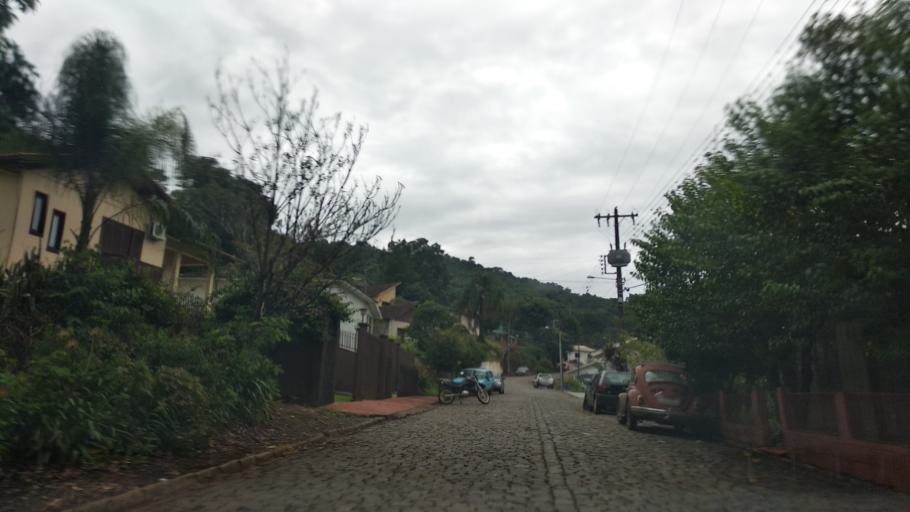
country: BR
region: Santa Catarina
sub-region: Videira
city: Videira
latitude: -27.1016
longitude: -51.2394
